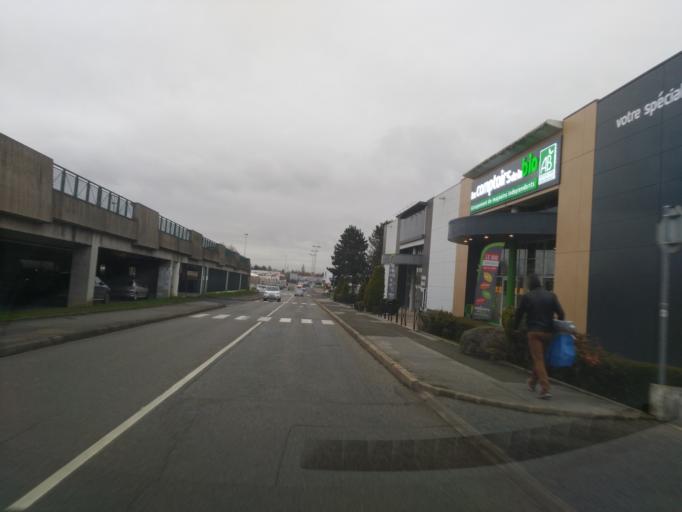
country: FR
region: Ile-de-France
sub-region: Departement des Yvelines
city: Plaisir
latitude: 48.8305
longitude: 1.9623
